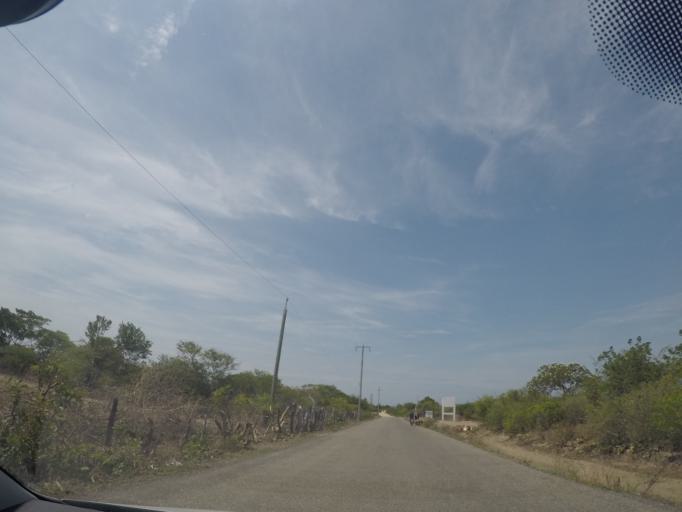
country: MX
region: Oaxaca
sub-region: Salina Cruz
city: Salina Cruz
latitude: 16.1939
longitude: -95.1192
